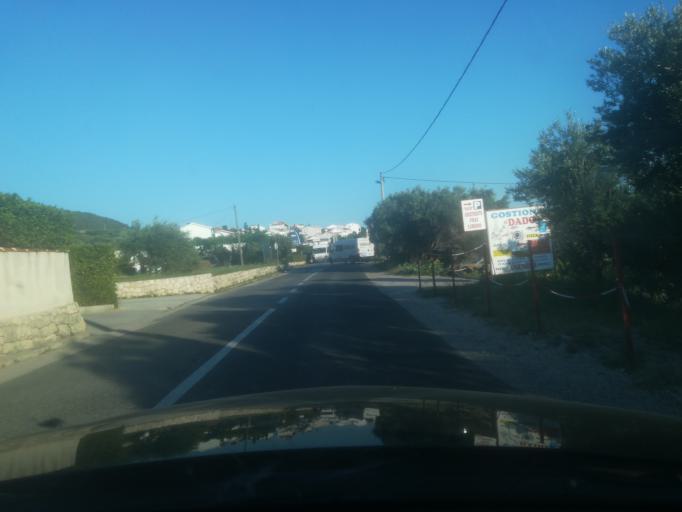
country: HR
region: Primorsko-Goranska
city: Banjol
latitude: 44.7488
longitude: 14.7879
